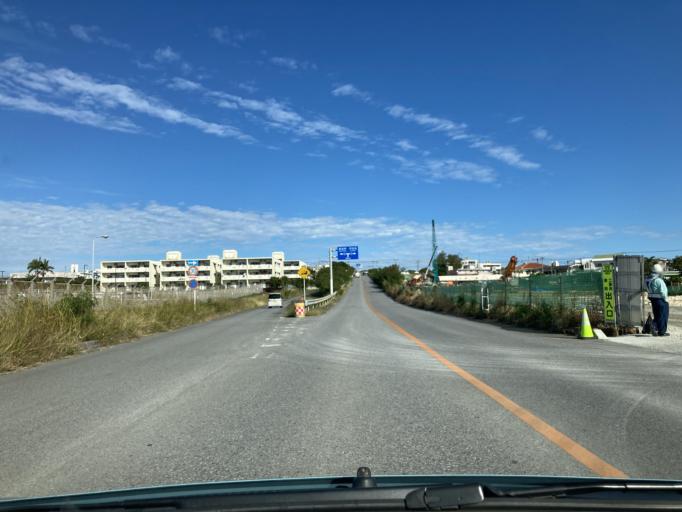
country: JP
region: Okinawa
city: Okinawa
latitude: 26.3783
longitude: 127.7455
